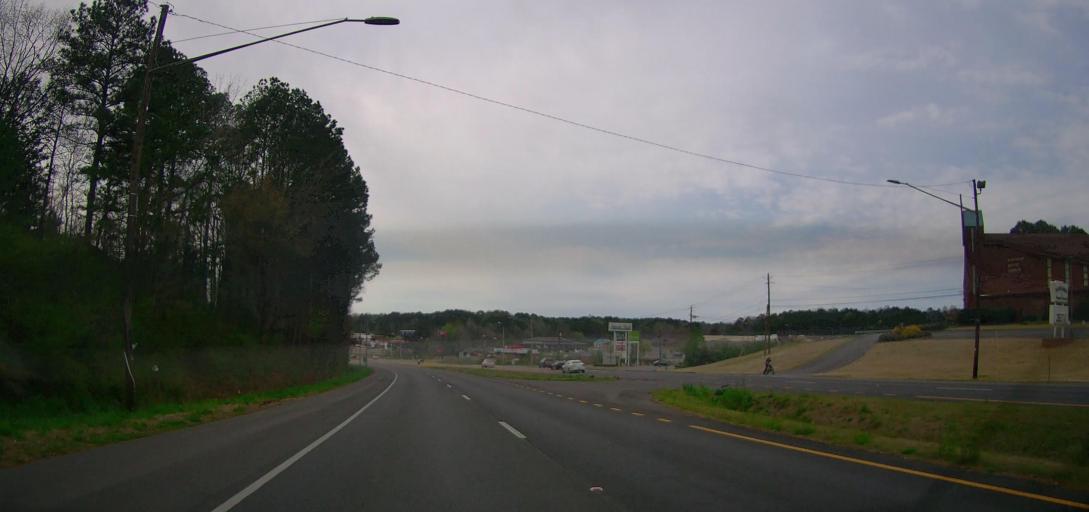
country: US
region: Alabama
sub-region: Walker County
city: Jasper
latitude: 33.8488
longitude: -87.2701
